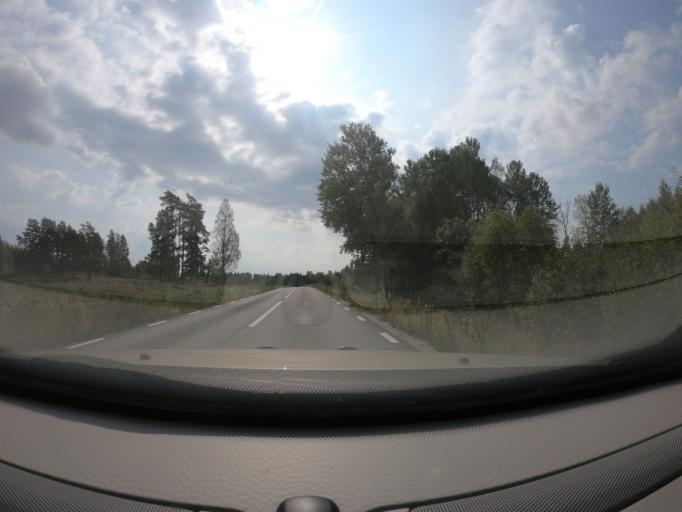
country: SE
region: Kronoberg
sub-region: Vaxjo Kommun
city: Braas
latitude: 57.1403
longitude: 14.9638
